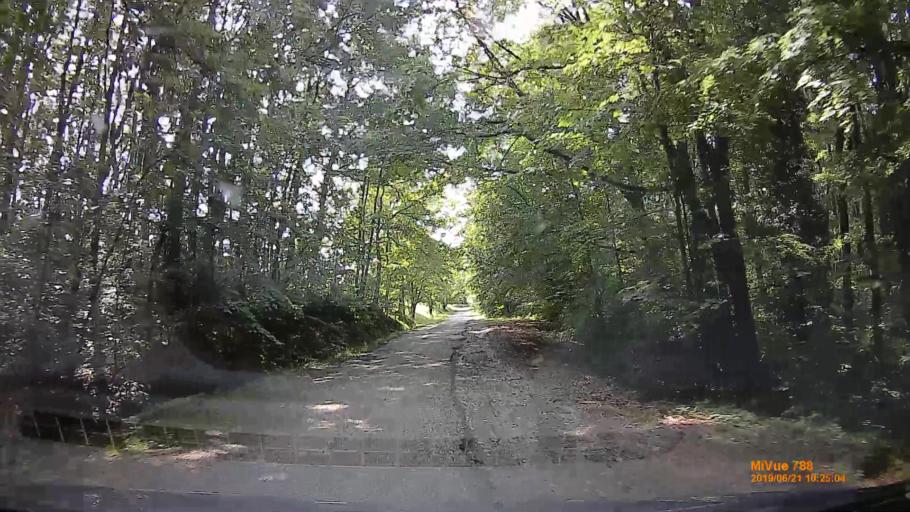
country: HU
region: Baranya
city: Buekkoesd
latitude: 46.1806
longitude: 17.9748
